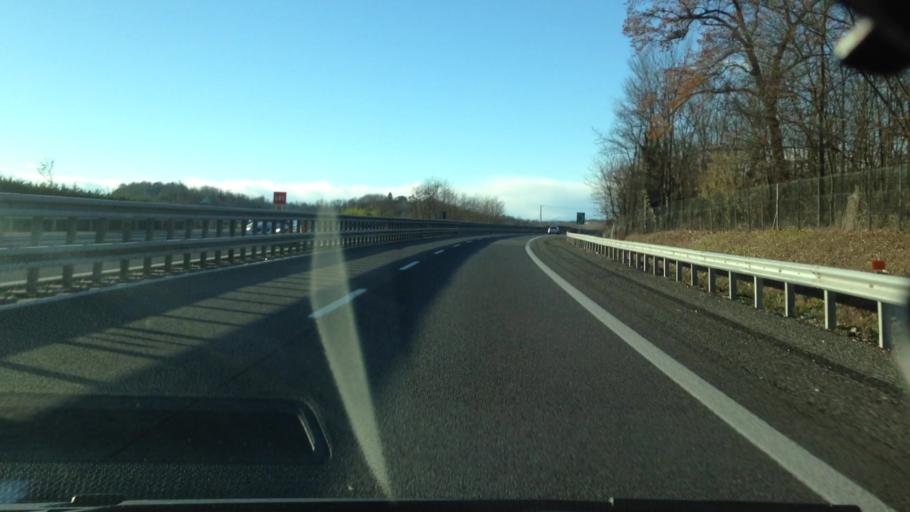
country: IT
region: Piedmont
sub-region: Provincia di Asti
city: Tigliole
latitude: 44.9019
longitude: 8.0658
